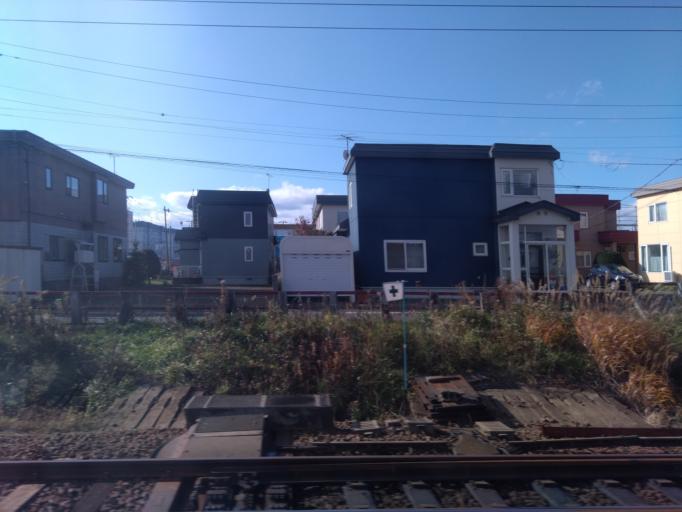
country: JP
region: Hokkaido
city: Kitahiroshima
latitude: 42.9176
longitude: 141.5735
